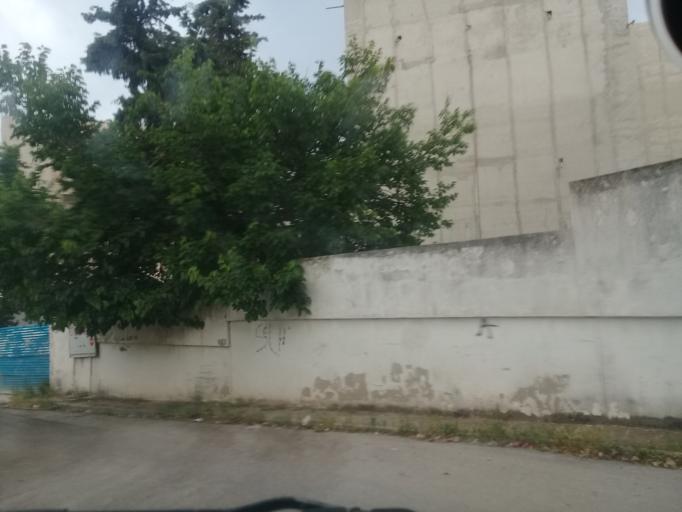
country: TN
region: Tunis
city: Sidi Bou Said
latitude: 36.8652
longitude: 10.3403
